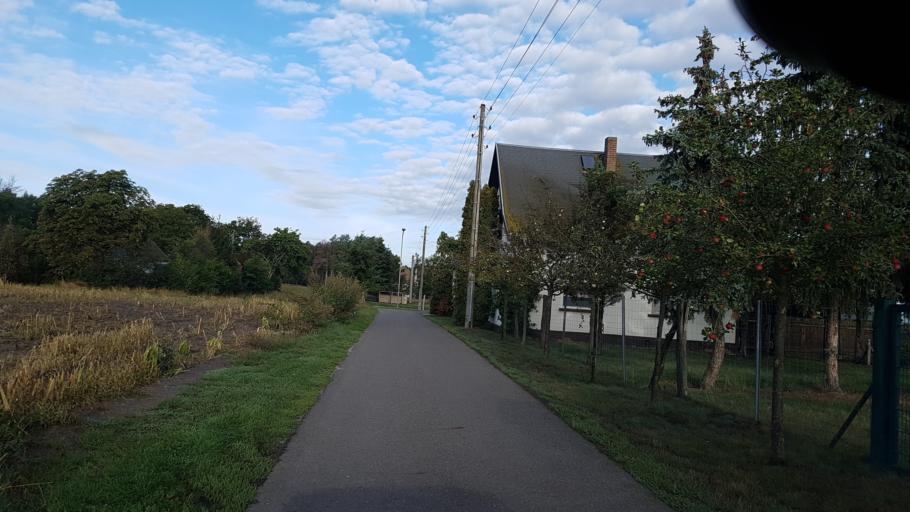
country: DE
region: Brandenburg
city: Welzow
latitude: 51.5571
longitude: 14.1717
